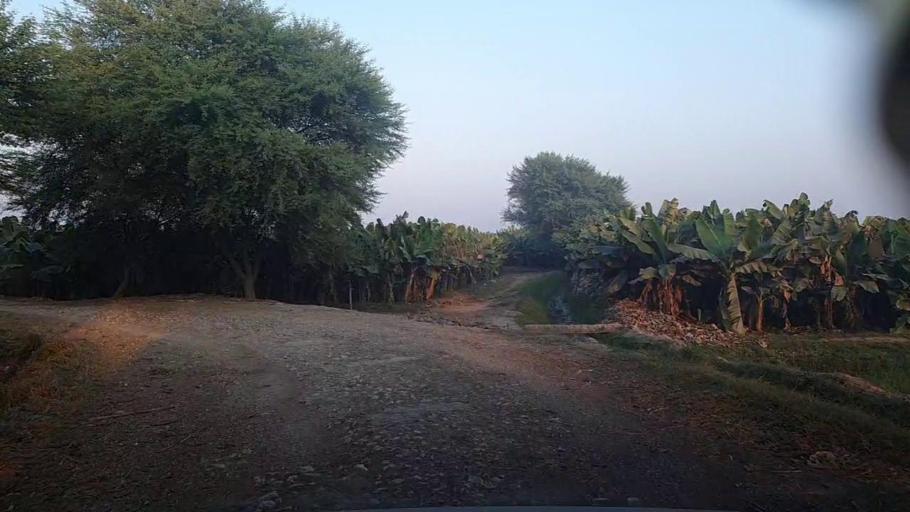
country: PK
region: Sindh
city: Karaundi
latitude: 26.8445
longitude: 68.3630
